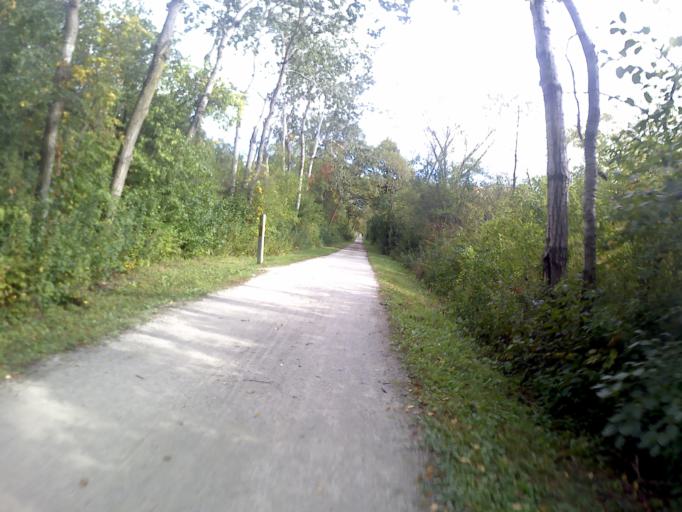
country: US
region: Illinois
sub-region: DuPage County
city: Winfield
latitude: 41.8917
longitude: -88.1584
